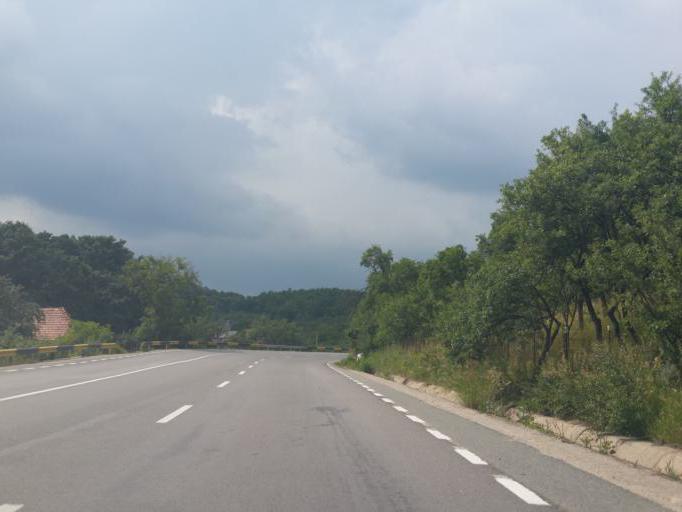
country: RO
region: Salaj
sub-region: Comuna Treznea
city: Treznea
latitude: 47.1331
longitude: 23.1303
